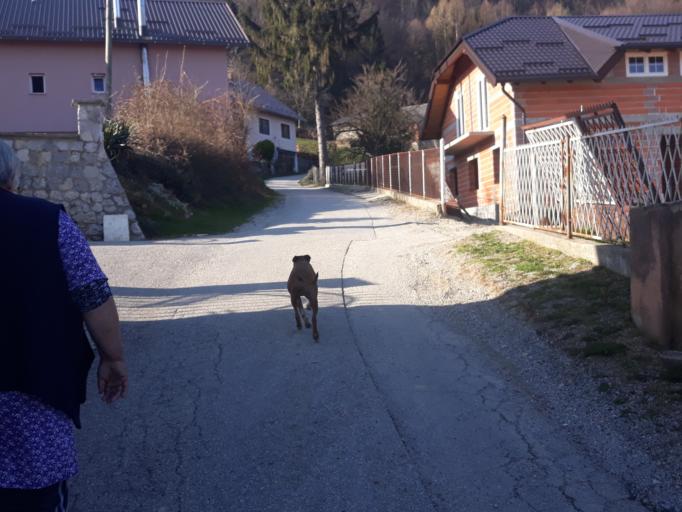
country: HR
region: Varazdinska
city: Ivanec
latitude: 46.1967
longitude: 16.1376
